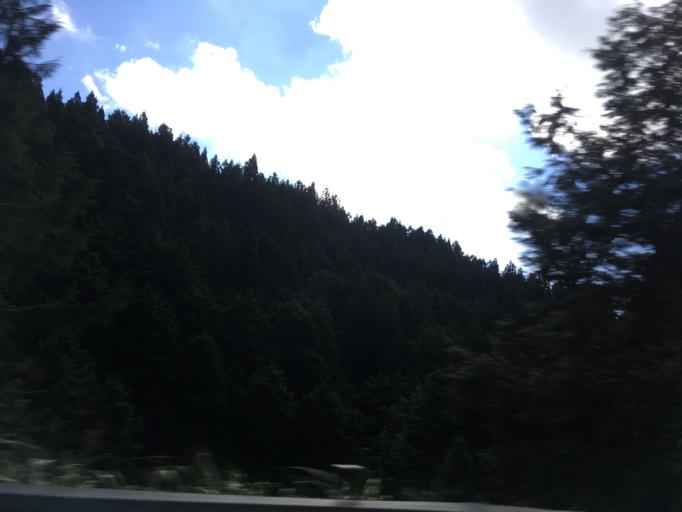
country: TW
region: Taiwan
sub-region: Yilan
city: Yilan
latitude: 24.5127
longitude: 121.5911
